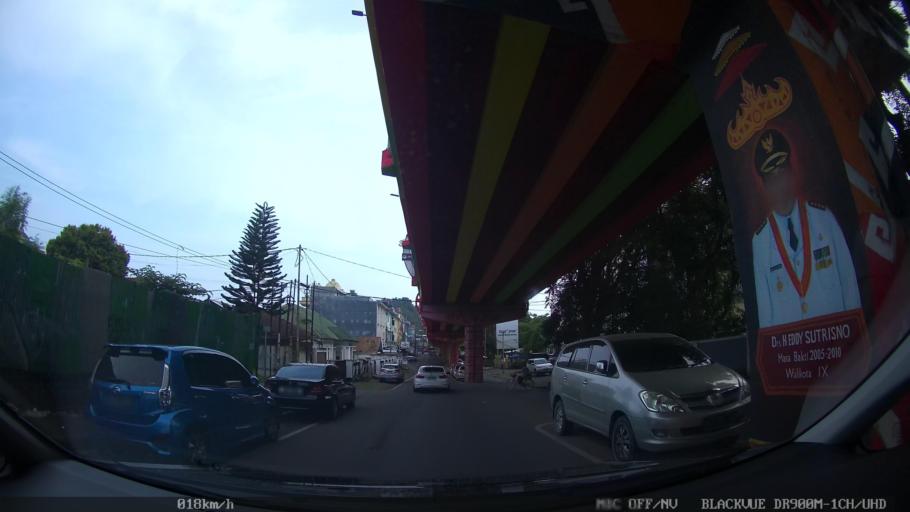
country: ID
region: Lampung
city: Bandarlampung
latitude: -5.4225
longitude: 105.2695
